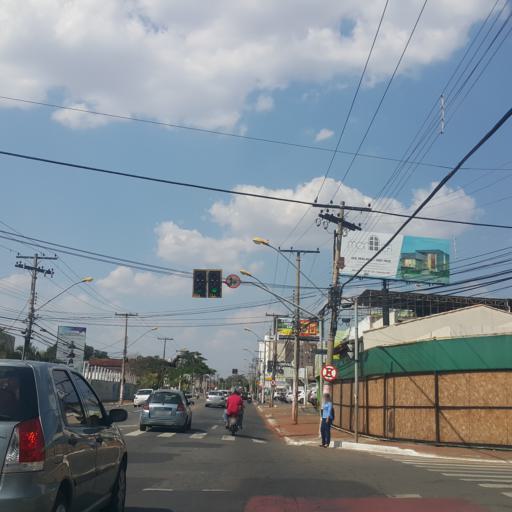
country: BR
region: Goias
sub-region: Goiania
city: Goiania
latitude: -16.6909
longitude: -49.2596
